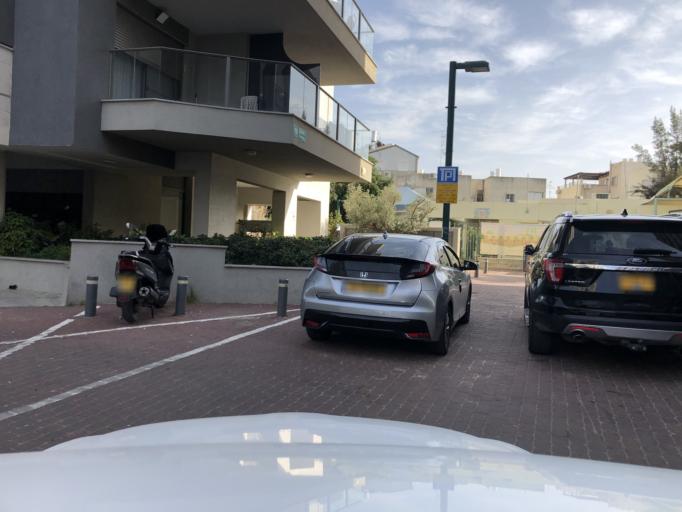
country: IL
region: Tel Aviv
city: Bene Beraq
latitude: 32.0776
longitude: 34.8267
